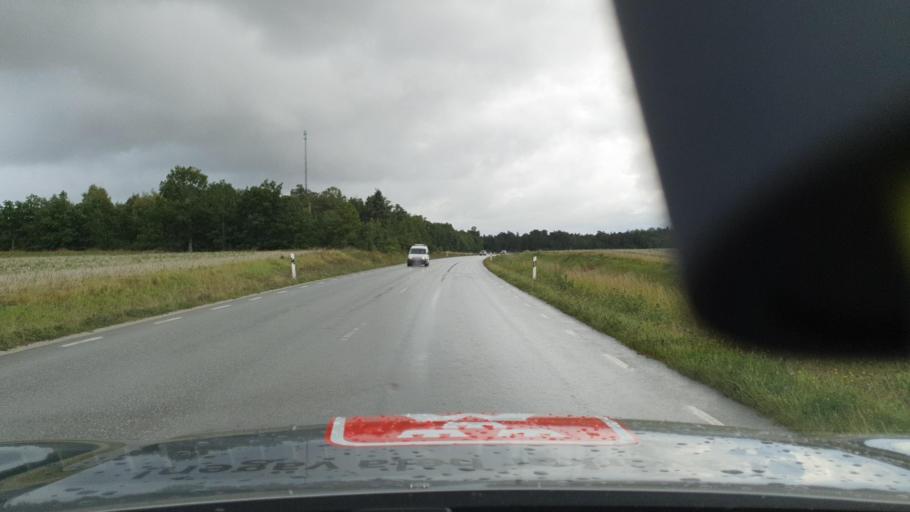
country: SE
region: Gotland
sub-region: Gotland
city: Hemse
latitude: 57.2227
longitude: 18.3699
